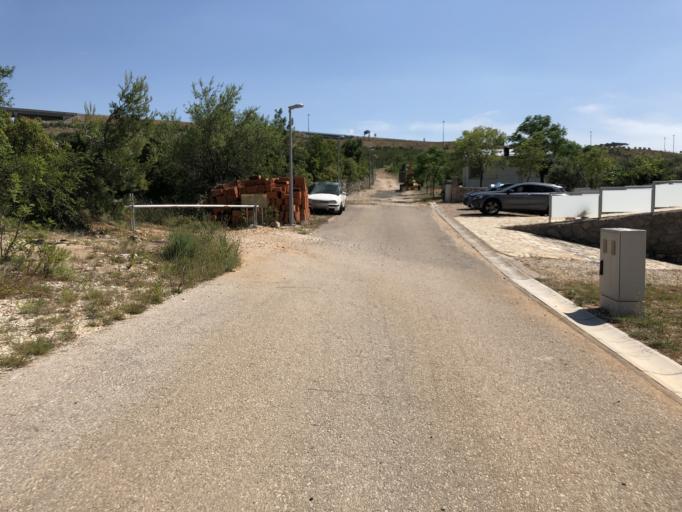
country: HR
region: Zadarska
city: Posedarje
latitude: 44.2441
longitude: 15.5363
